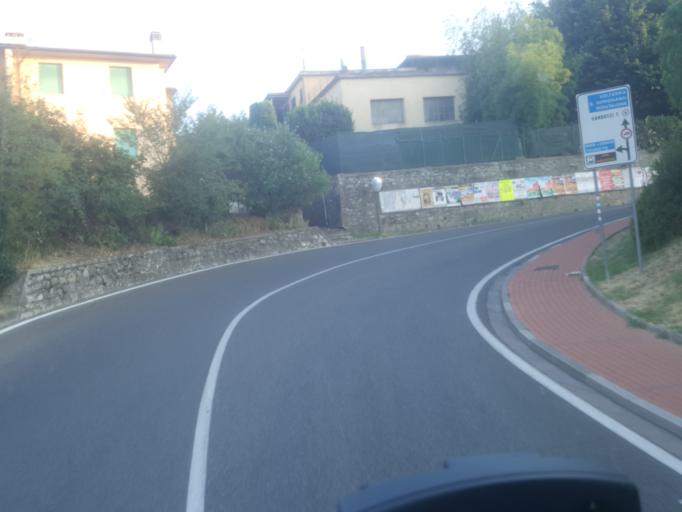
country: IT
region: Tuscany
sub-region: Province of Florence
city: Gambassi Terme
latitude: 43.5413
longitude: 10.9555
